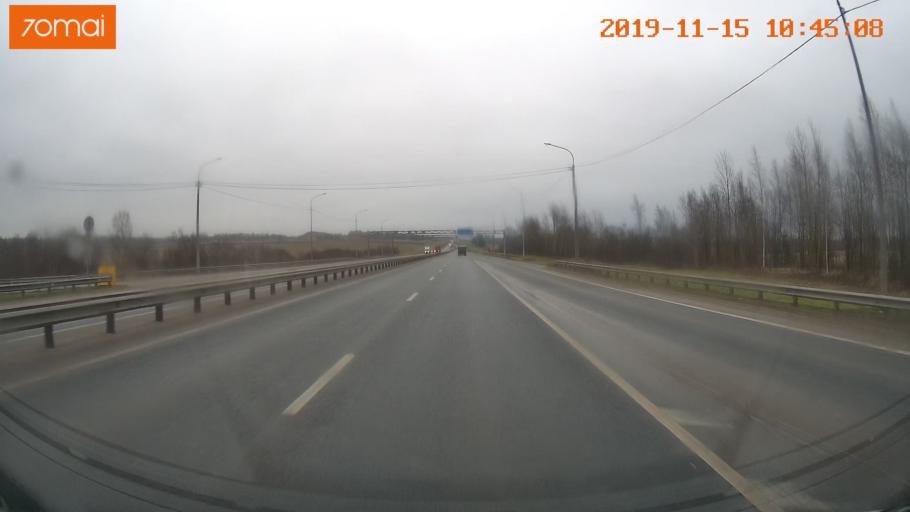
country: RU
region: Vologda
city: Sheksna
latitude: 59.2112
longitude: 38.5791
